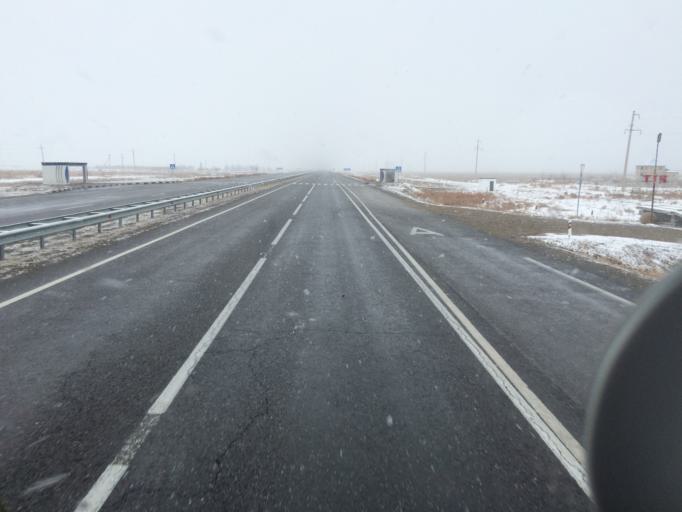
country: KZ
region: Ongtustik Qazaqstan
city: Turkestan
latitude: 43.4574
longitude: 67.9333
